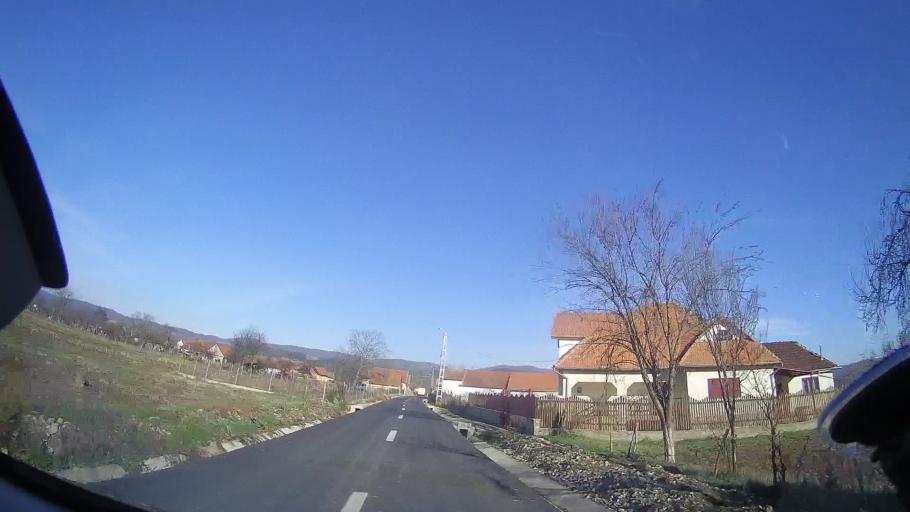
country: RO
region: Bihor
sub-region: Comuna Auseu
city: Auseu
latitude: 47.0191
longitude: 22.4933
